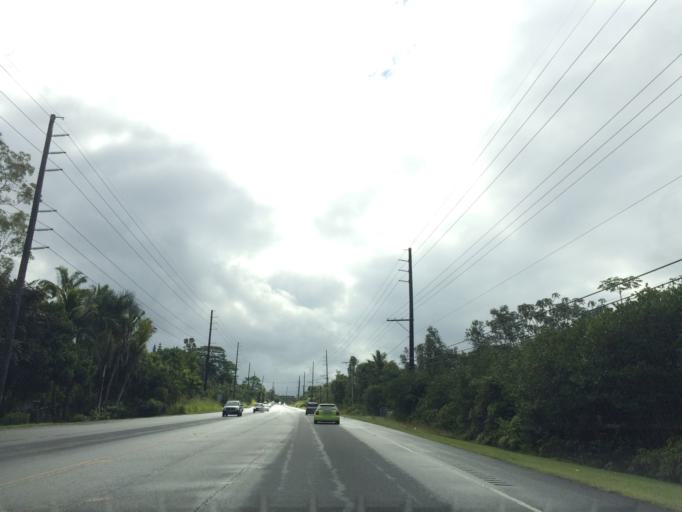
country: US
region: Hawaii
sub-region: Hawaii County
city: Ainaloa
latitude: 19.5481
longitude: -154.9801
